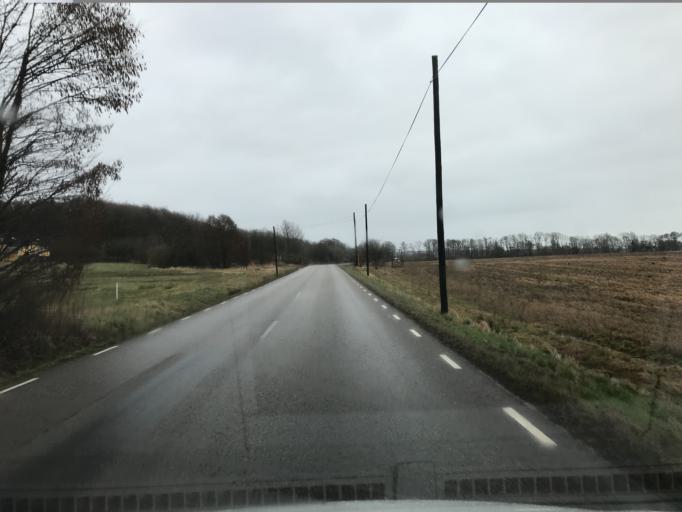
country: SE
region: Skane
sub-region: Bastads Kommun
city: Forslov
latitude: 56.3388
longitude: 12.8789
